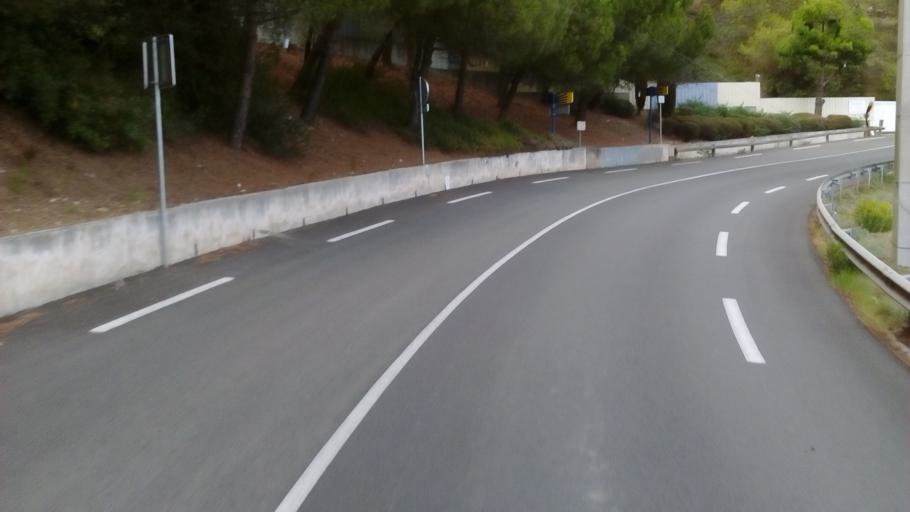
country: MC
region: Commune de Monaco
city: Saint-Roman
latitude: 43.7551
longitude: 7.4308
